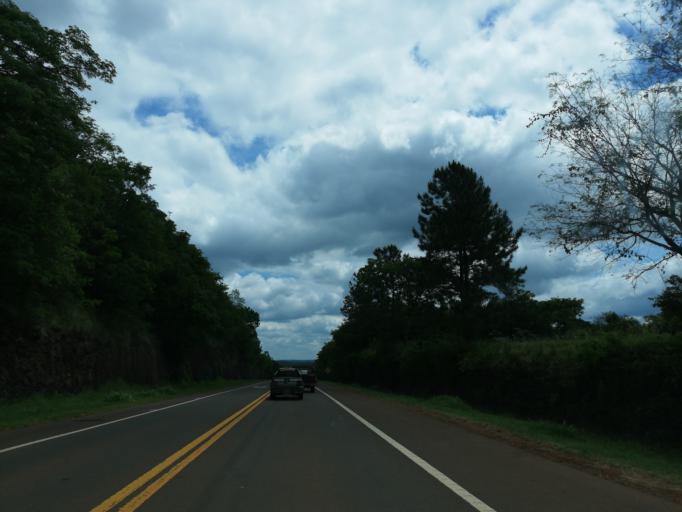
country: AR
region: Misiones
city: Arroyo del Medio
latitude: -27.6445
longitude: -55.4053
